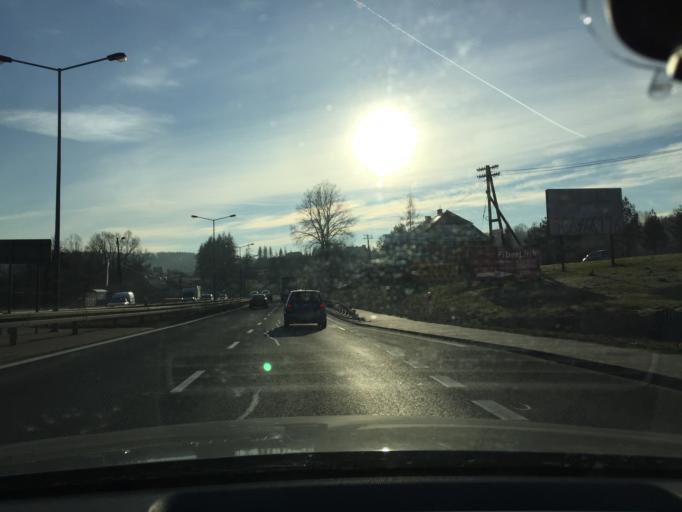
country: PL
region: Lesser Poland Voivodeship
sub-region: Powiat krakowski
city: Mogilany
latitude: 49.9258
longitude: 19.8830
